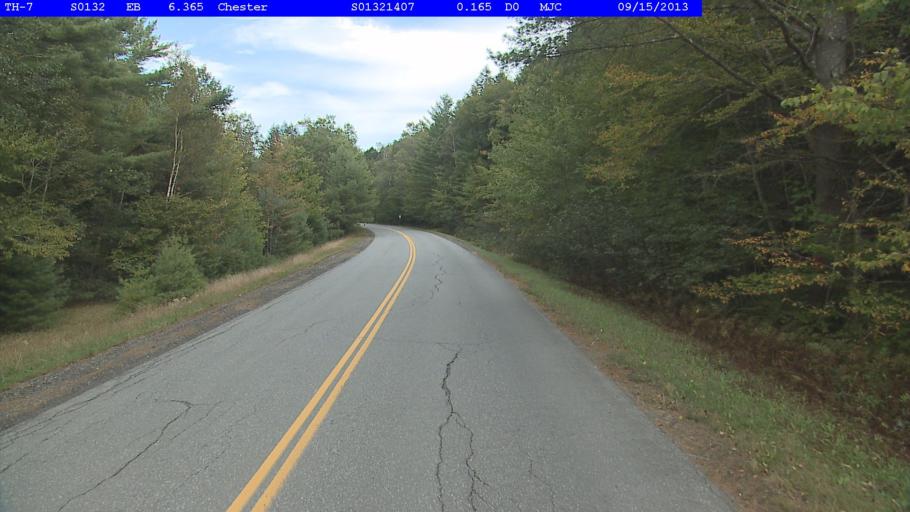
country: US
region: Vermont
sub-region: Windsor County
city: Chester
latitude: 43.2707
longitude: -72.6808
